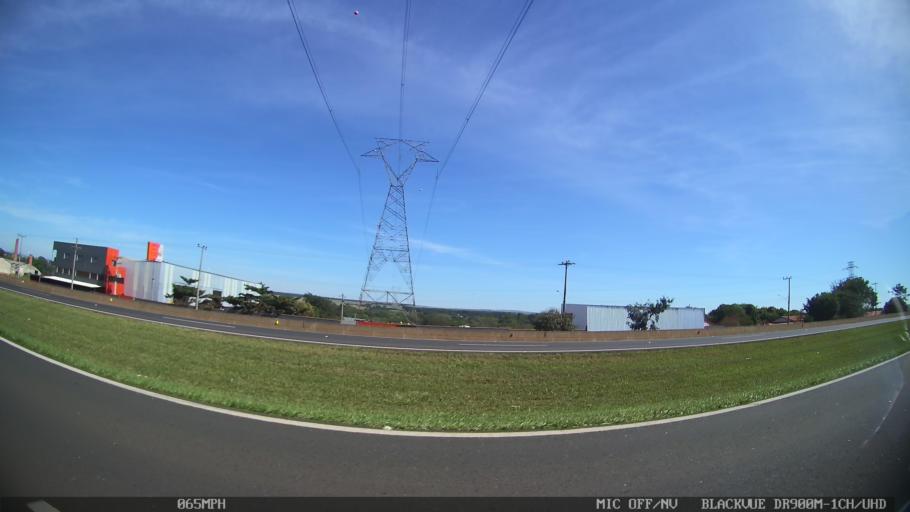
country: BR
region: Sao Paulo
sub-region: Porto Ferreira
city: Porto Ferreira
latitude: -21.8289
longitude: -47.4952
